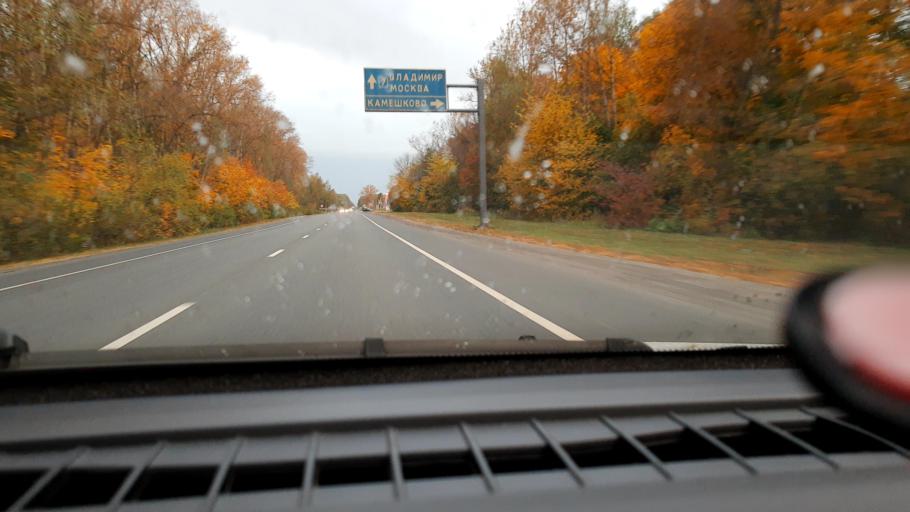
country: RU
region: Vladimir
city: Orgtrud
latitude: 56.2027
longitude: 40.7659
